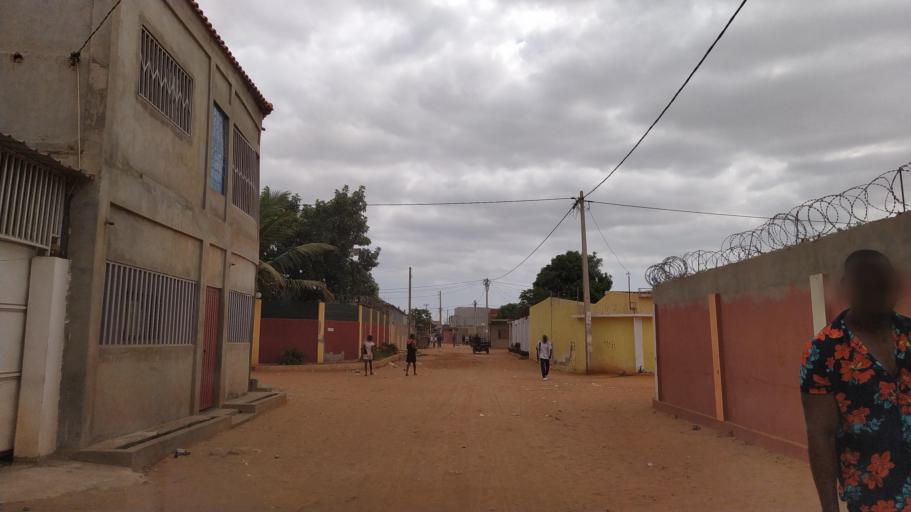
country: AO
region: Luanda
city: Luanda
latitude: -8.9340
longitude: 13.2572
